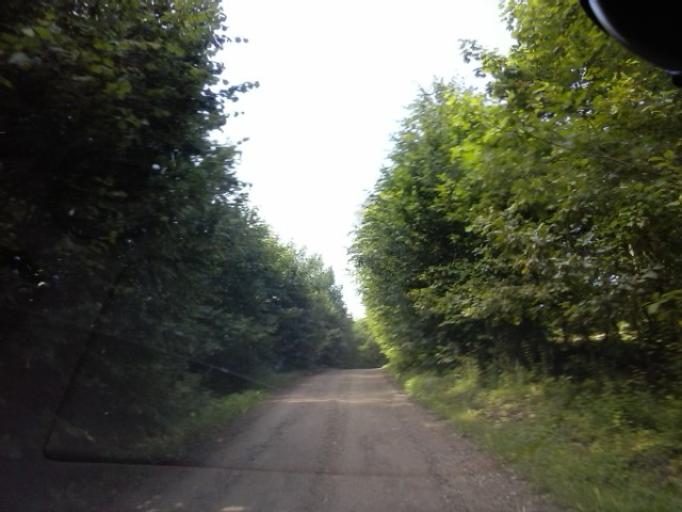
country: EE
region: Polvamaa
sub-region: Polva linn
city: Polva
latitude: 58.2574
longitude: 26.9504
